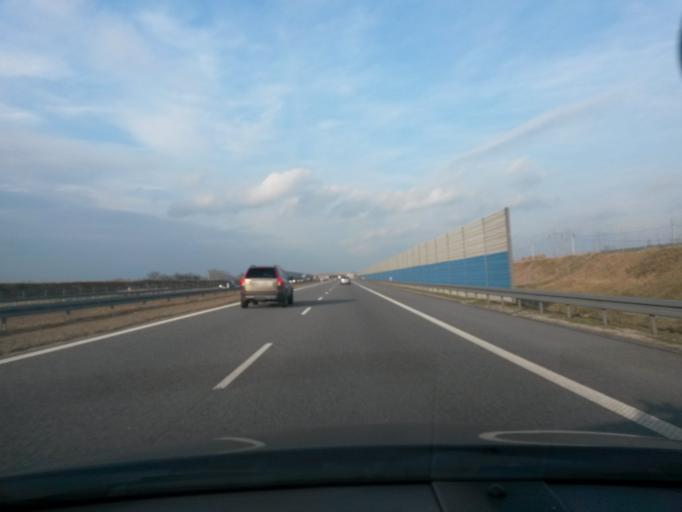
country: PL
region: Lodz Voivodeship
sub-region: Powiat brzezinski
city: Dmosin
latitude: 51.9409
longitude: 19.8217
